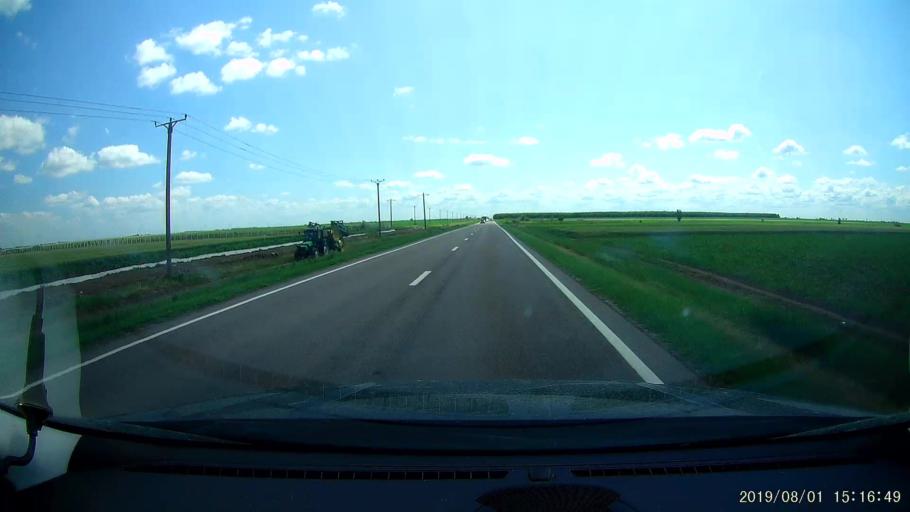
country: RO
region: Braila
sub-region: Comuna Unirea
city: Unirea
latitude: 45.1399
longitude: 27.8465
